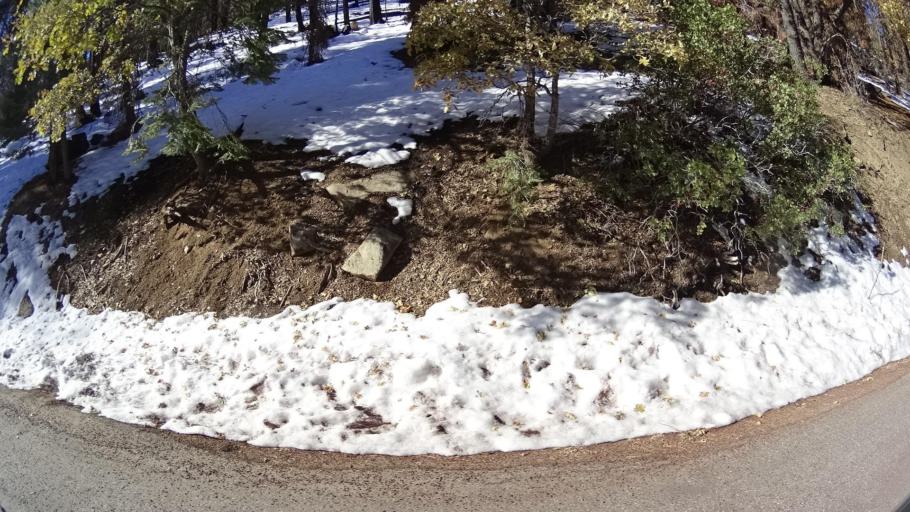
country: US
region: California
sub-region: Kern County
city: Alta Sierra
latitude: 35.7281
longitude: -118.5576
